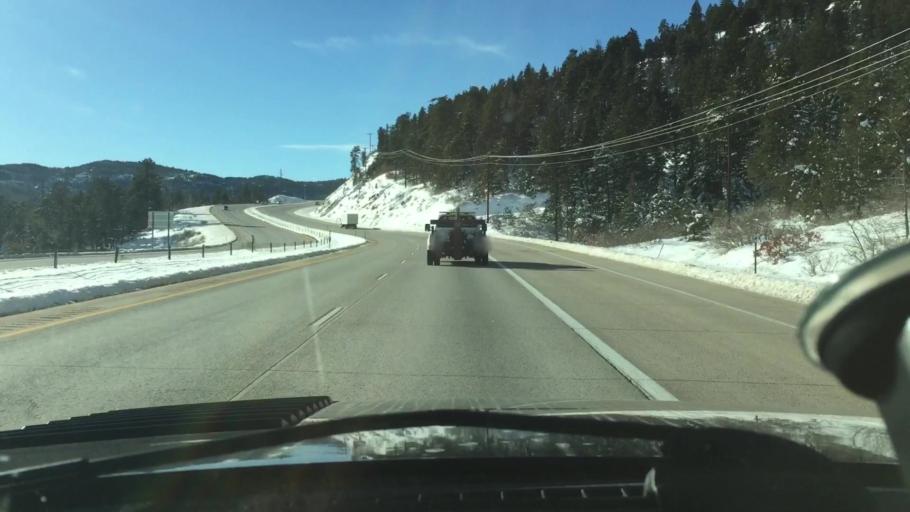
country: US
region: Colorado
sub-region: Jefferson County
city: Indian Hills
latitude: 39.5615
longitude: -105.2397
